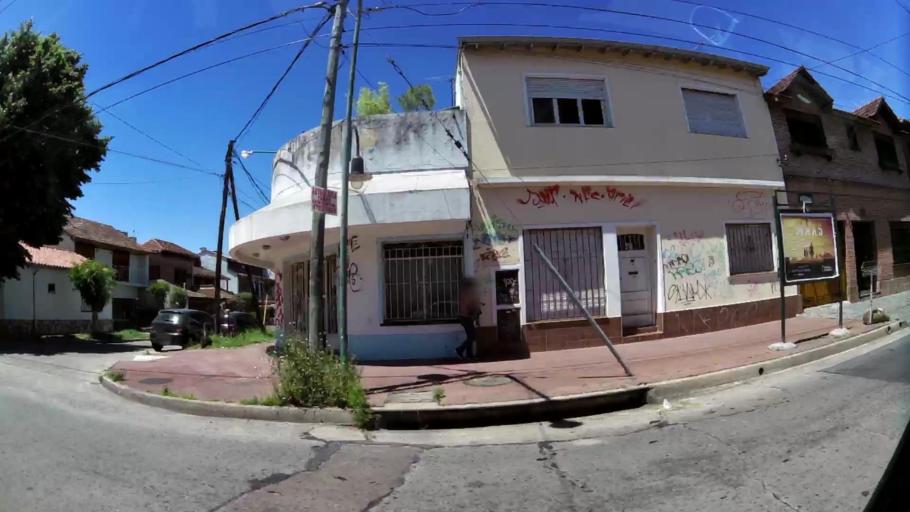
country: AR
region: Buenos Aires
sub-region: Partido de Vicente Lopez
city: Olivos
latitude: -34.5004
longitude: -58.5035
